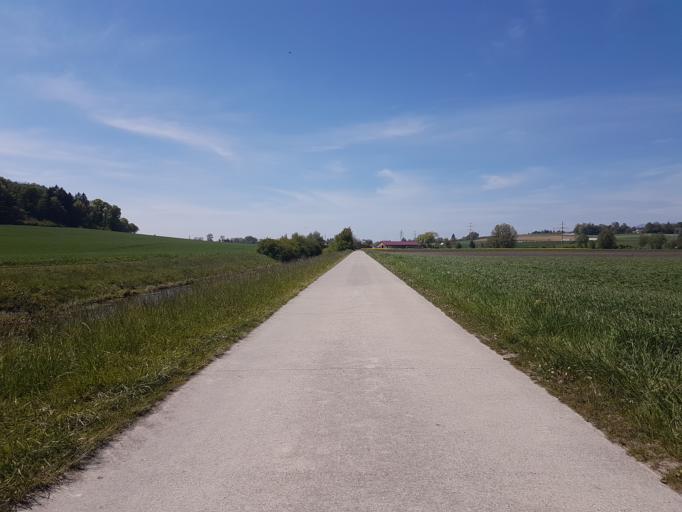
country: CH
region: Neuchatel
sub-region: Neuchatel District
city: Cornaux
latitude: 47.0322
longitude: 7.0397
